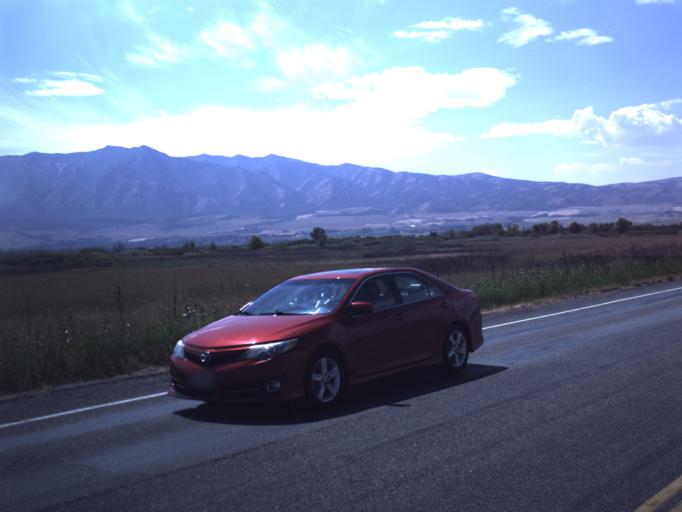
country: US
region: Utah
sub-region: Cache County
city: Benson
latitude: 41.7419
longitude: -111.9125
